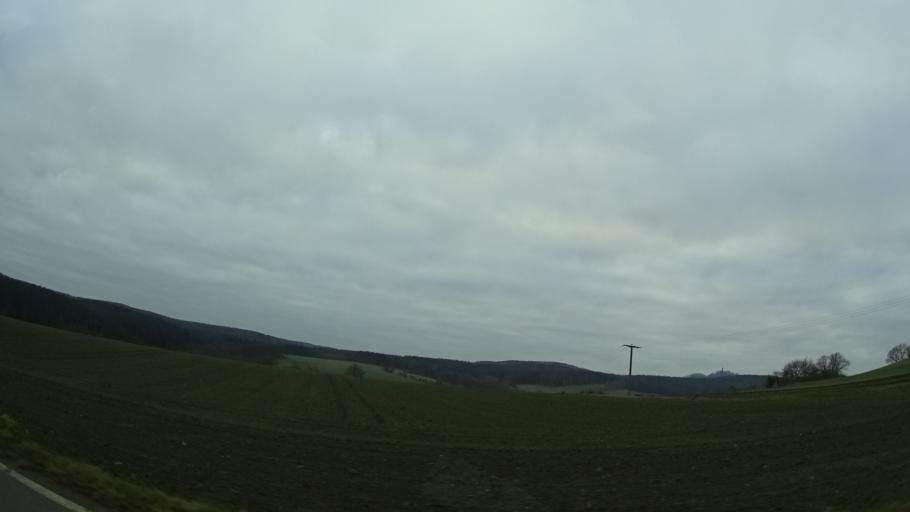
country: DE
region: Thuringia
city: Unterbodnitz
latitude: 50.8253
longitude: 11.6533
